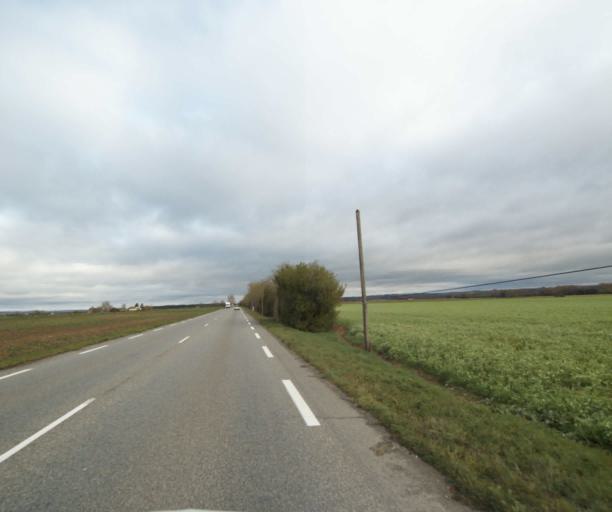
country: FR
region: Midi-Pyrenees
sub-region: Departement de l'Ariege
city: Saverdun
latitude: 43.2558
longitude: 1.5630
